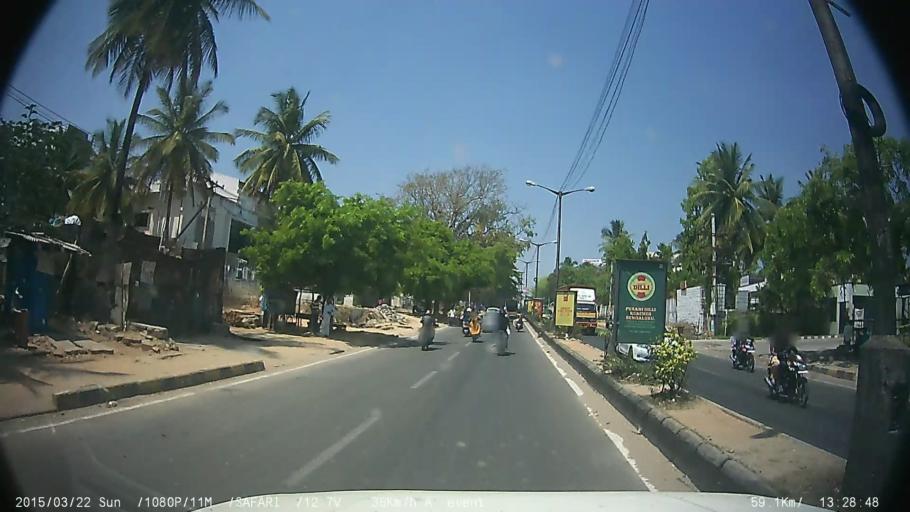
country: IN
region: Karnataka
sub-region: Bangalore Urban
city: Bangalore
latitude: 12.8849
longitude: 77.5965
